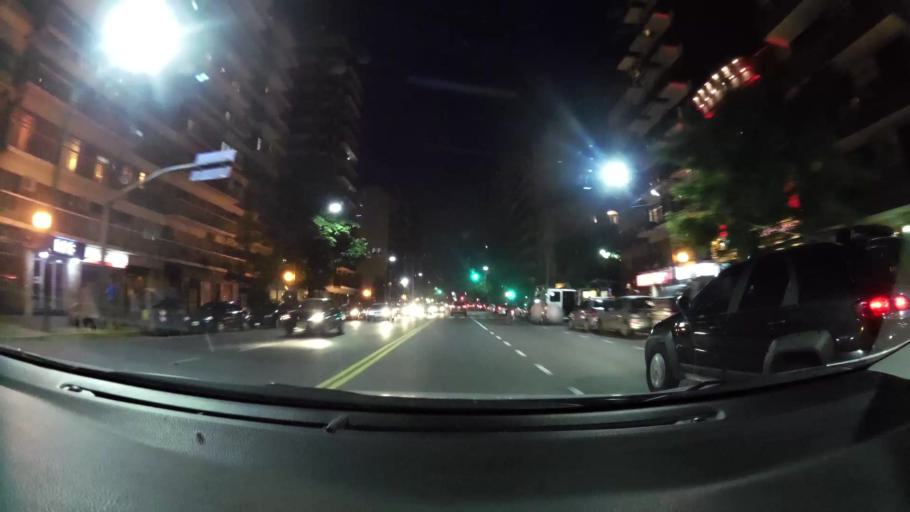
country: AR
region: Buenos Aires F.D.
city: Colegiales
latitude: -34.5679
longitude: -58.4585
